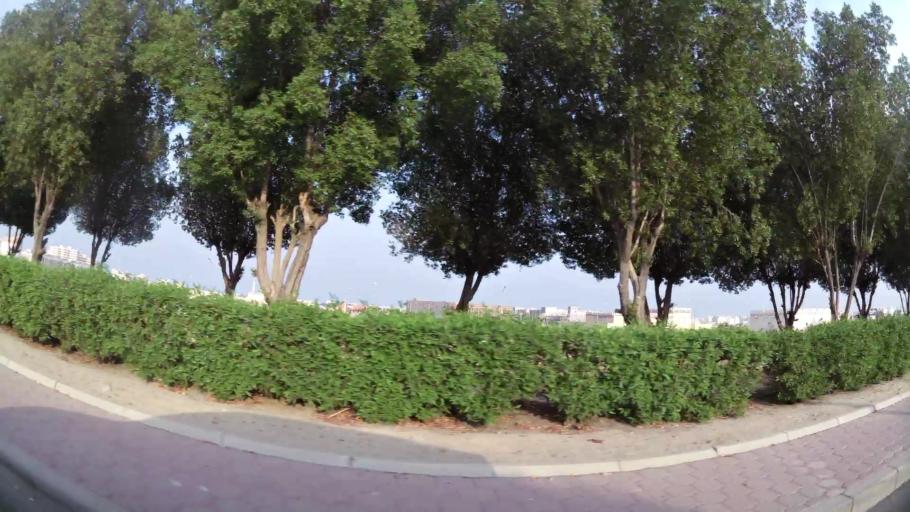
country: KW
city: Al Funaytis
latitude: 29.2428
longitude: 48.0829
